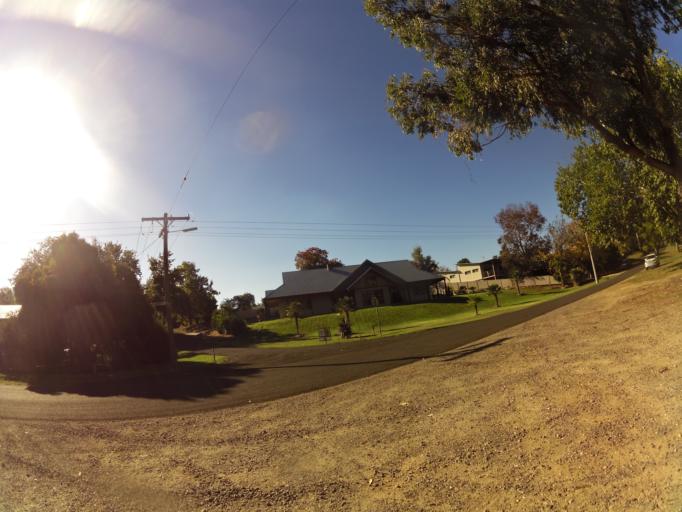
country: AU
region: Victoria
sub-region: Murrindindi
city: Alexandra
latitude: -37.1870
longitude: 145.7123
